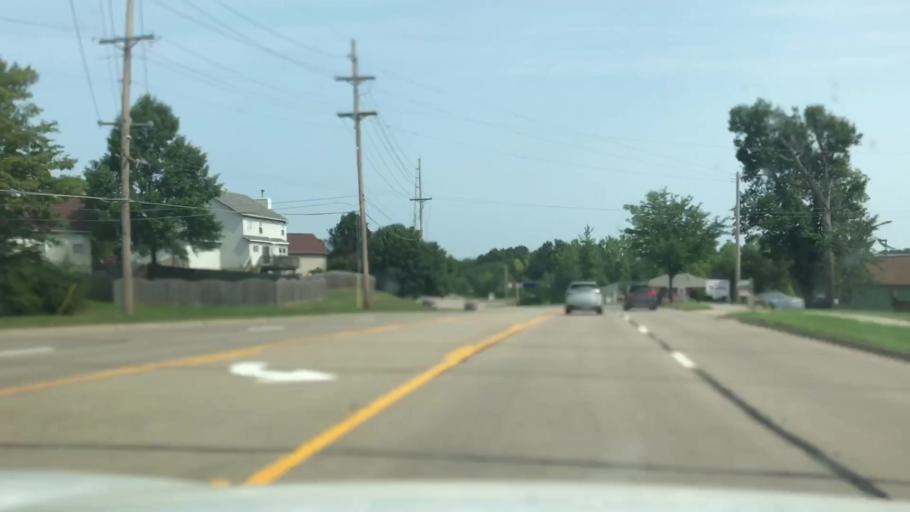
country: US
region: Missouri
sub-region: Saint Charles County
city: Dardenne Prairie
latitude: 38.7933
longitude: -90.7364
